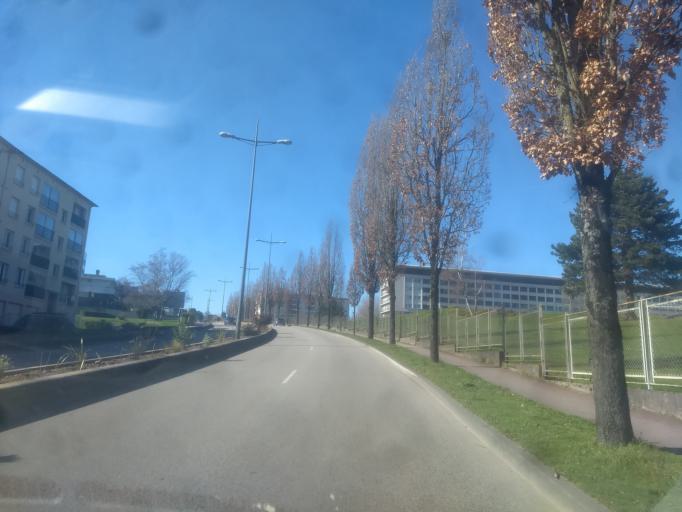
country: FR
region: Limousin
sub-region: Departement de la Haute-Vienne
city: Limoges
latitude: 45.8218
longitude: 1.2434
